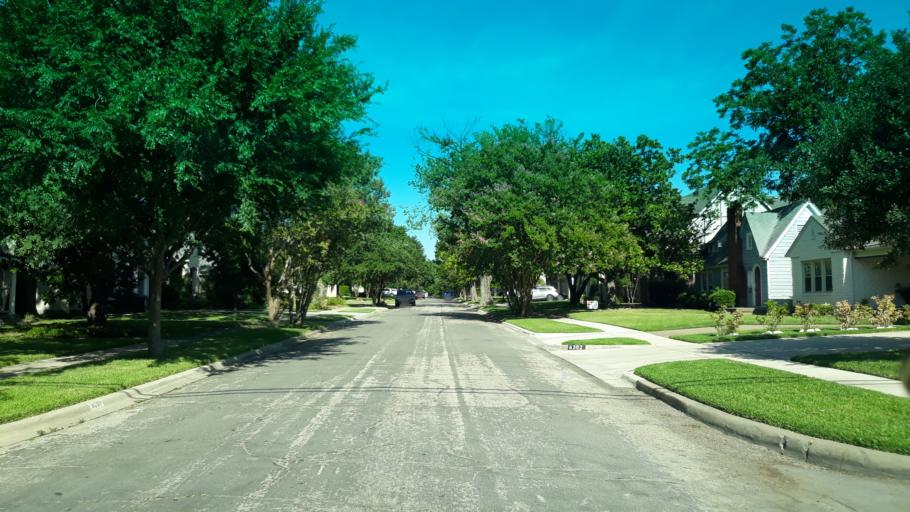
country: US
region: Texas
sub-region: Dallas County
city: Highland Park
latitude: 32.8201
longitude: -96.7560
